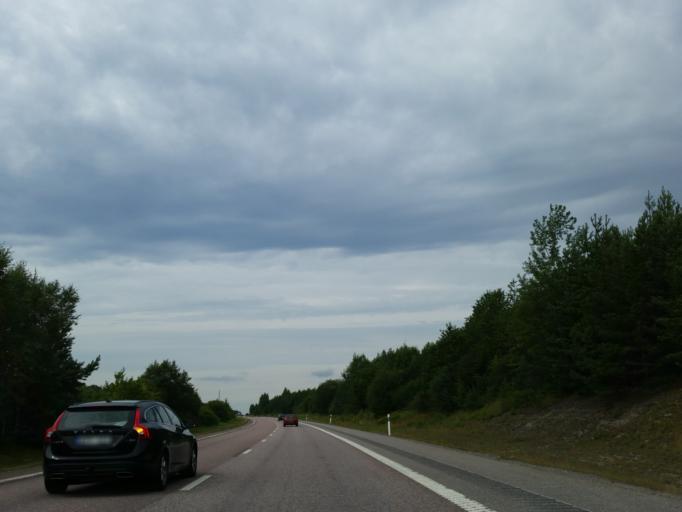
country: SE
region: Soedermanland
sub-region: Strangnas Kommun
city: Mariefred
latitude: 59.2207
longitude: 17.2881
